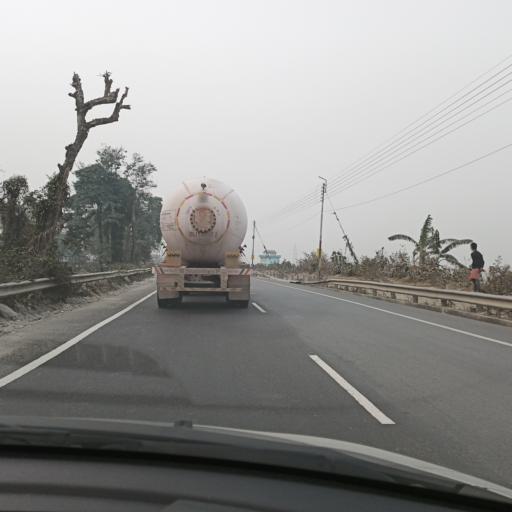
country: IN
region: West Bengal
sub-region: Darjiling
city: Shiliguri
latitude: 26.6519
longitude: 88.4067
